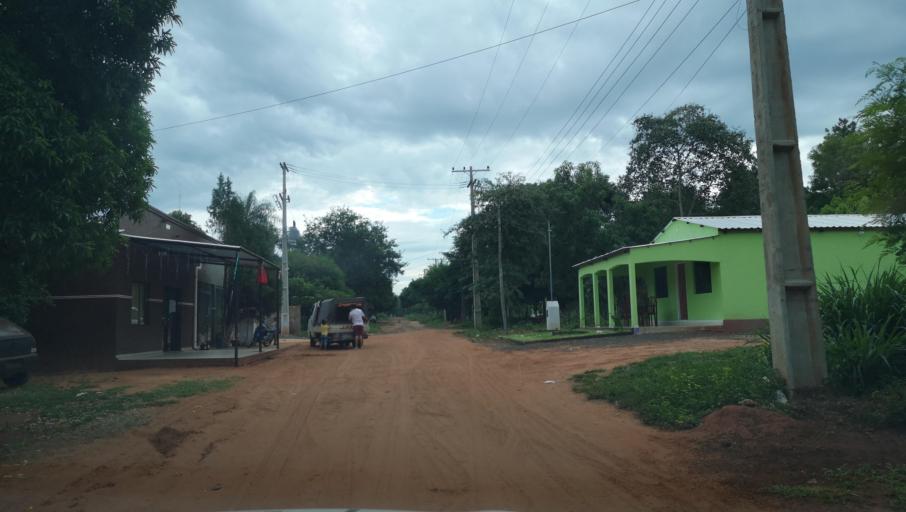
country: PY
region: San Pedro
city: Capiibary
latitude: -24.7244
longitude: -56.0186
